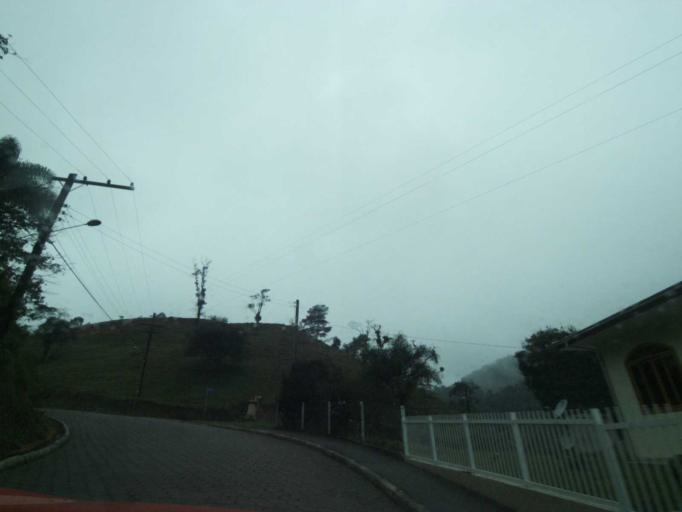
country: BR
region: Santa Catarina
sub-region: Anitapolis
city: Anitapolis
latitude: -27.9096
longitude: -49.1311
